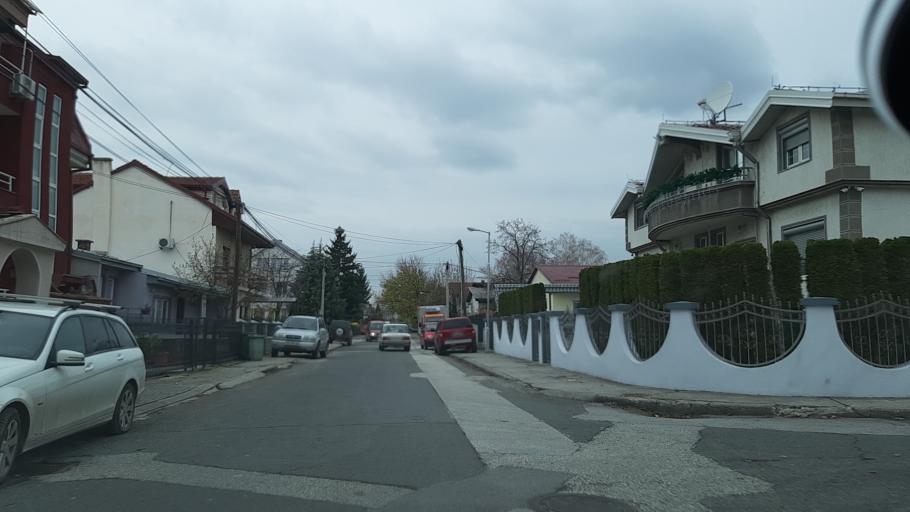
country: MK
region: Kisela Voda
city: Usje
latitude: 41.9712
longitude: 21.4738
